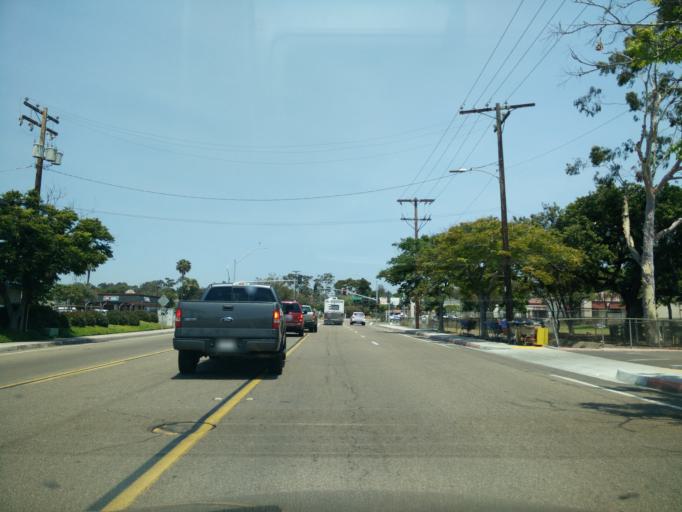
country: US
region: California
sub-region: San Diego County
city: Chula Vista
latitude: 32.6502
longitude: -117.0891
